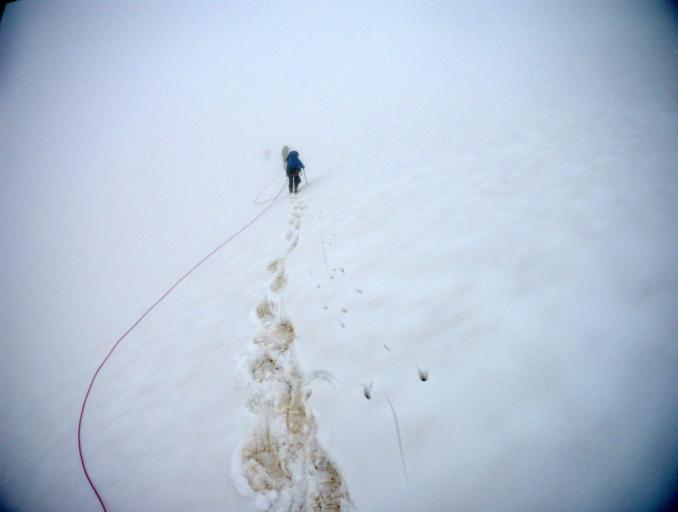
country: RU
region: Kabardino-Balkariya
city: Terskol
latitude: 43.3752
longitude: 42.4790
